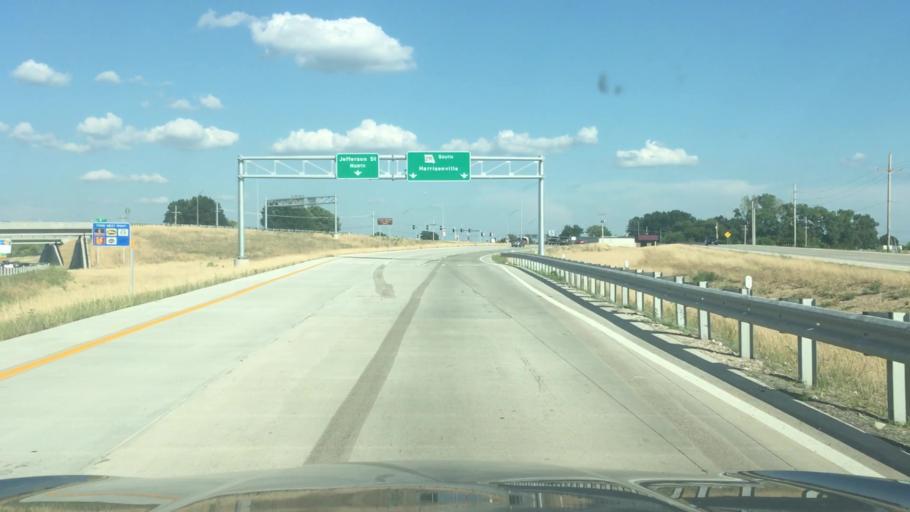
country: US
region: Missouri
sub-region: Jackson County
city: Lees Summit
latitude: 38.9034
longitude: -94.3793
